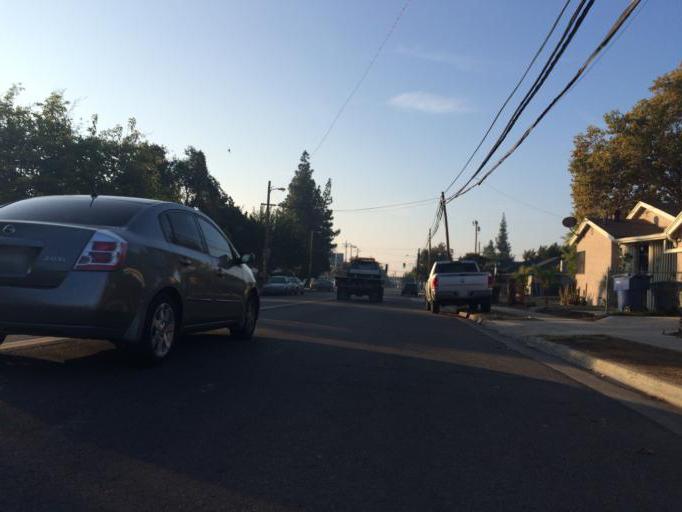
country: US
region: California
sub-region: Fresno County
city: Fresno
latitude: 36.7591
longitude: -119.7635
